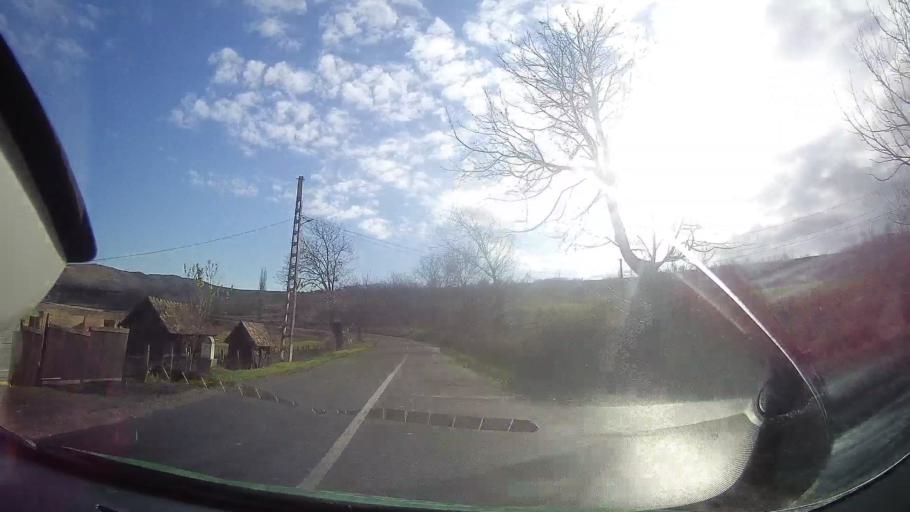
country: RO
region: Mures
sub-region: Comuna Iclanzel
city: Iclanzel
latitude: 46.5269
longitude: 24.2803
